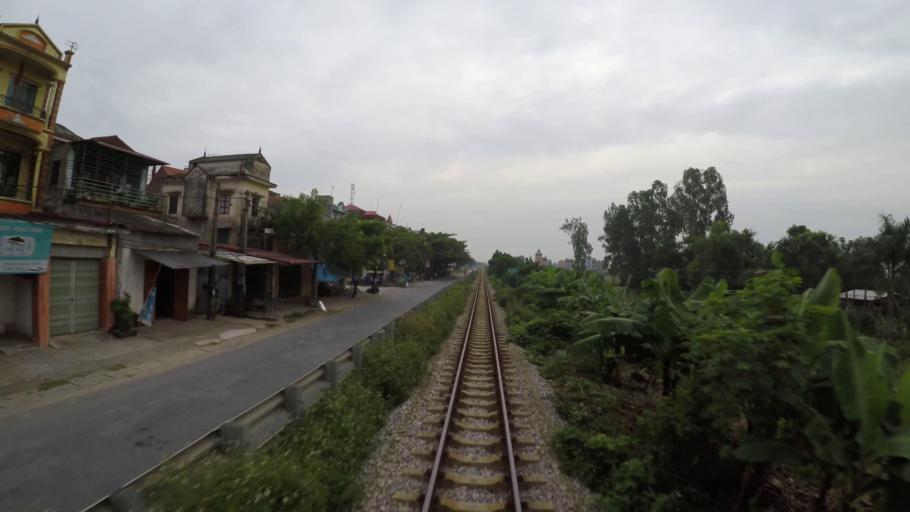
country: VN
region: Hung Yen
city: Ban Yen Nhan
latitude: 20.9671
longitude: 106.1077
